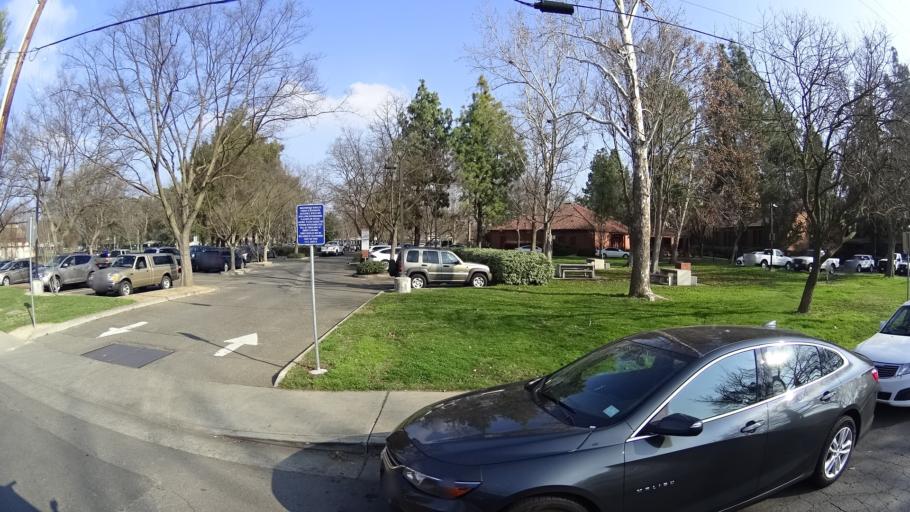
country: US
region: California
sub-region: Yolo County
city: Davis
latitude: 38.5470
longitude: -121.7478
